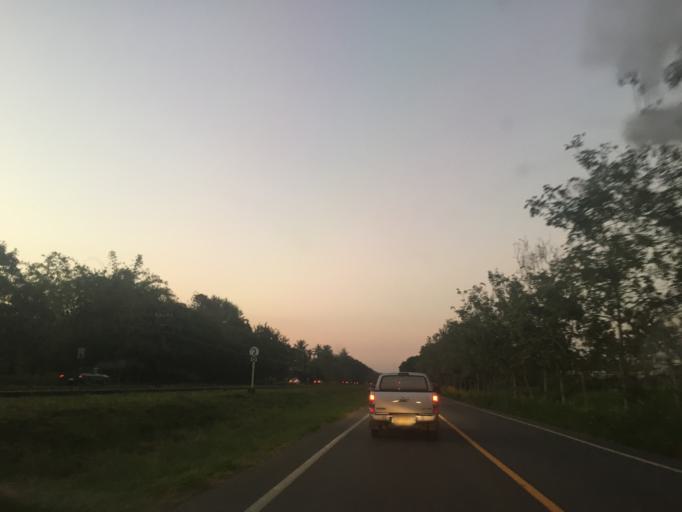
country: TH
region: Chiang Mai
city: Saraphi
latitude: 18.7037
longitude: 99.0447
